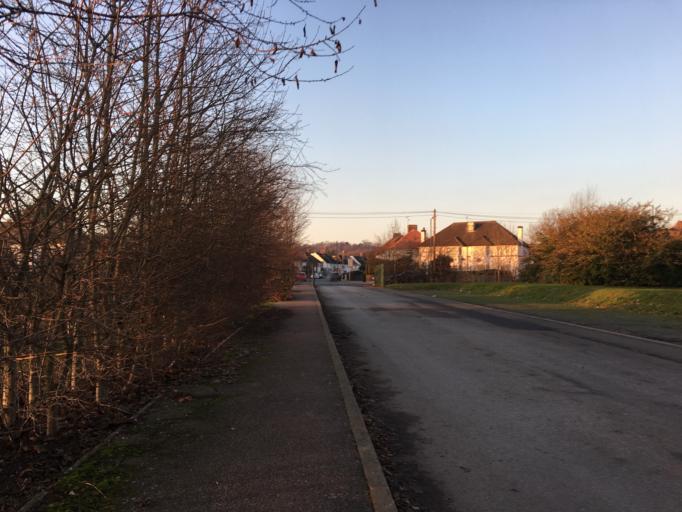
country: GB
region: England
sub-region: Greater London
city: Hendon
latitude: 51.6081
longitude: -0.2252
